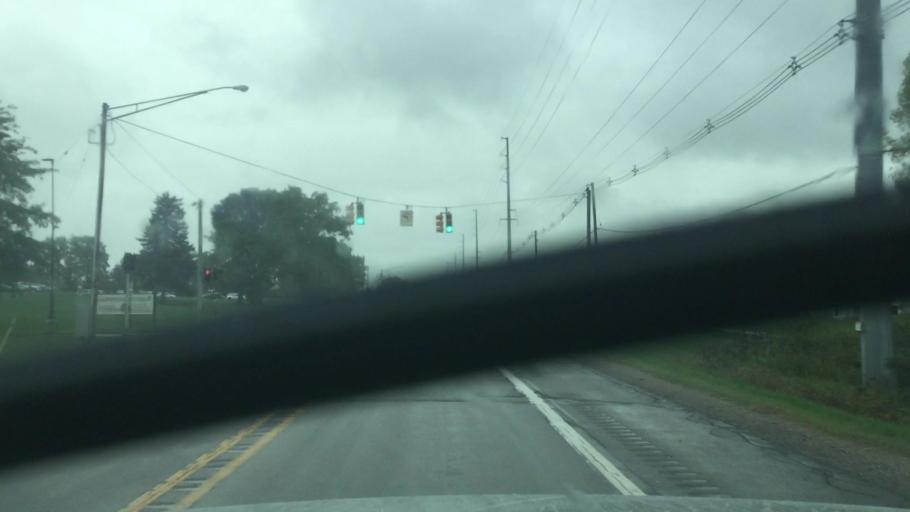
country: US
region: Michigan
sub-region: Livingston County
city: Brighton
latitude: 42.6324
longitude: -83.7665
